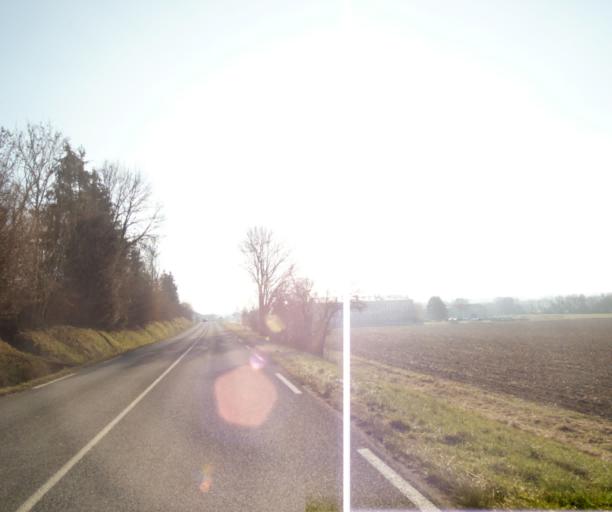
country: FR
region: Champagne-Ardenne
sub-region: Departement de la Haute-Marne
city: Wassy
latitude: 48.5074
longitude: 4.9412
